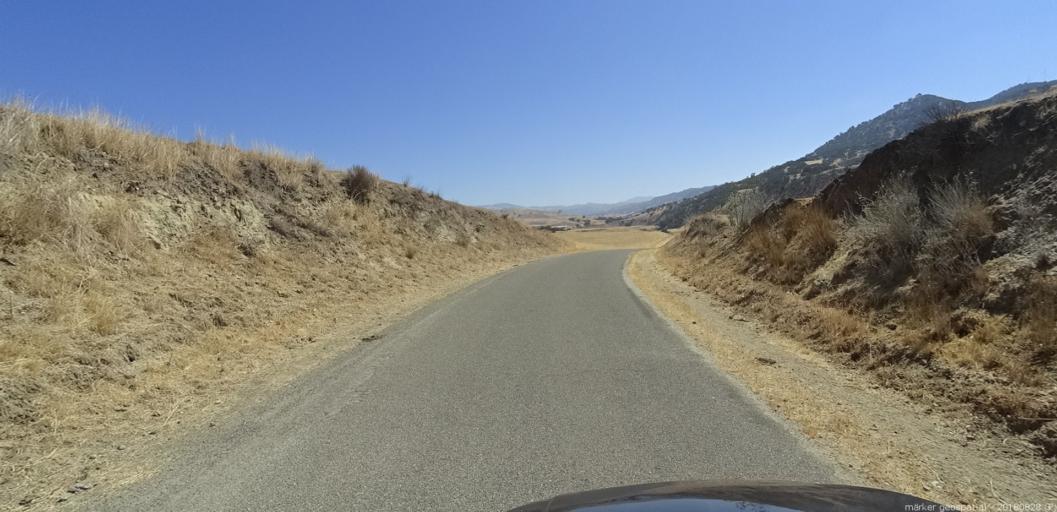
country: US
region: California
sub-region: San Luis Obispo County
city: San Miguel
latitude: 36.0645
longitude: -120.7925
